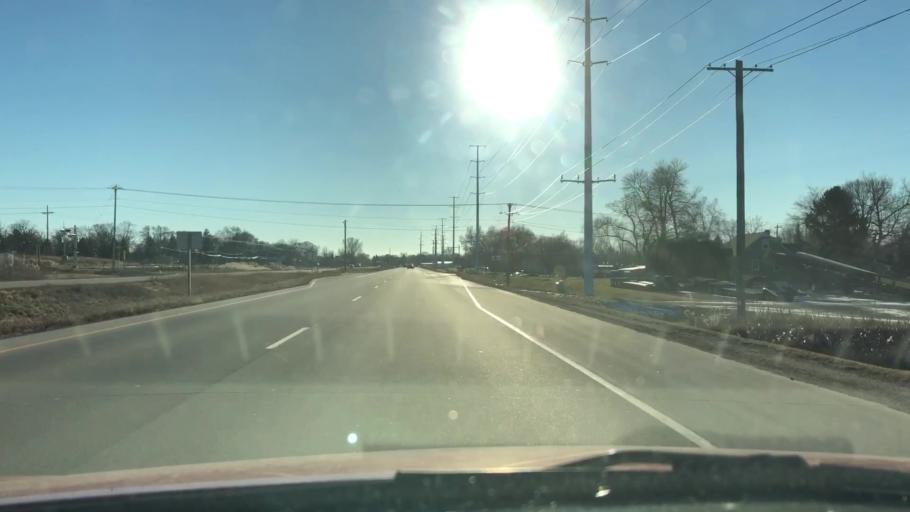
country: US
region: Wisconsin
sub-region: Brown County
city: De Pere
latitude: 44.4632
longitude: -88.0717
